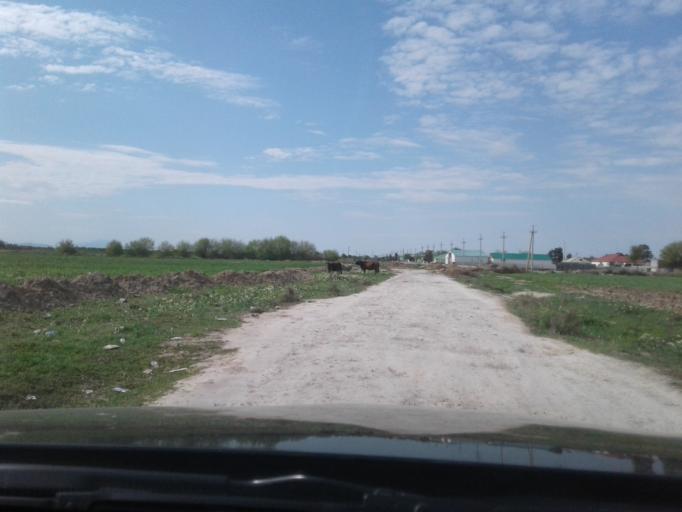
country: TM
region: Ahal
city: Ashgabat
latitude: 37.9797
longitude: 58.2903
